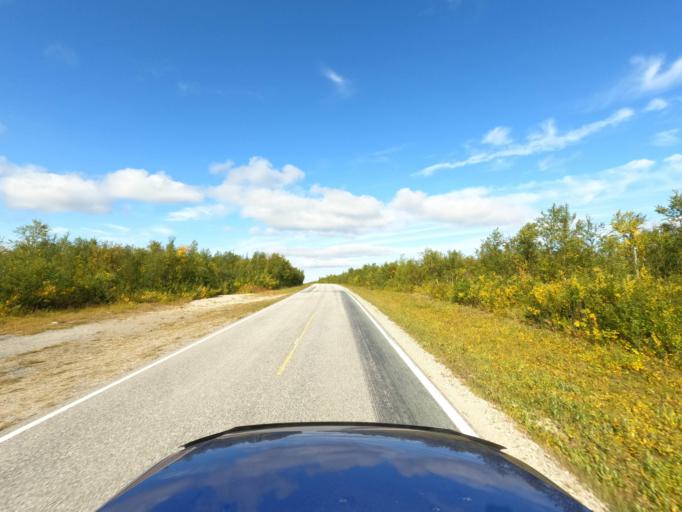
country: NO
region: Finnmark Fylke
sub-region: Karasjok
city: Karasjohka
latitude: 69.5858
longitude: 25.3467
